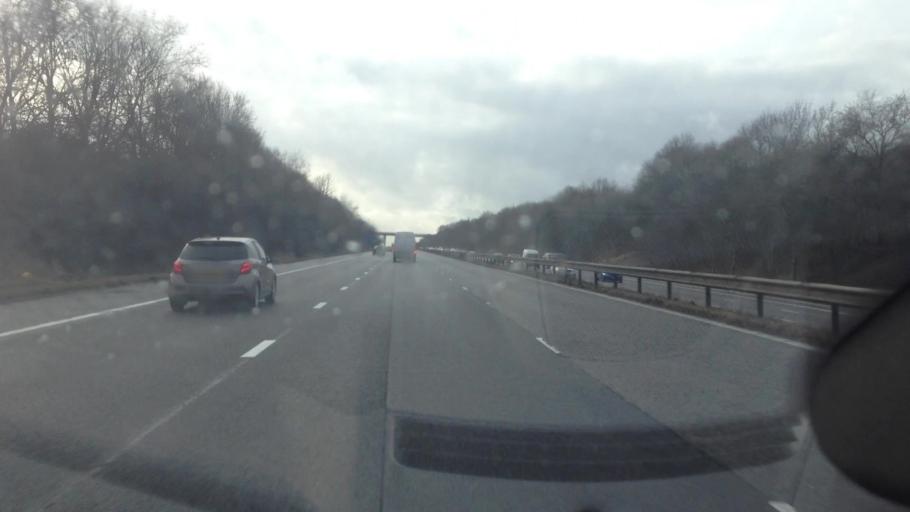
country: GB
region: England
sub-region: City and Borough of Wakefield
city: Crigglestone
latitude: 53.6257
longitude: -1.5436
